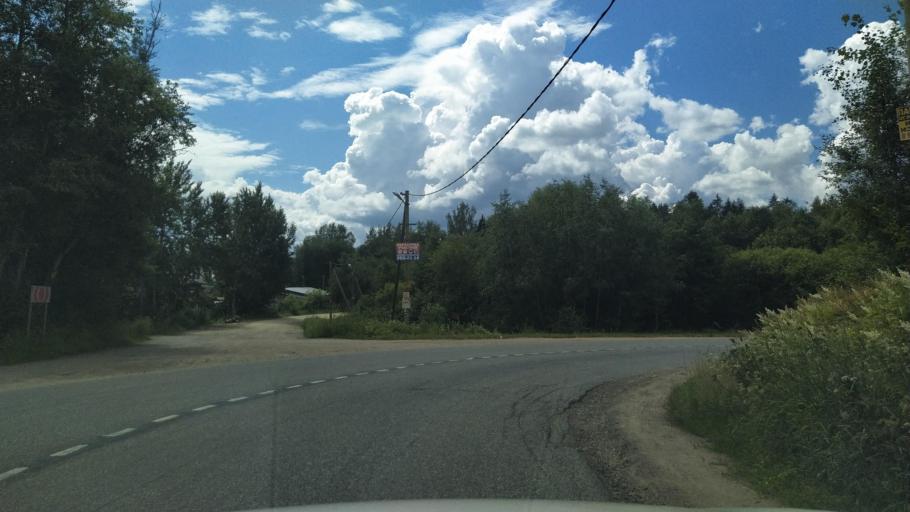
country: RU
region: Leningrad
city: Rozhdestveno
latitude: 59.3443
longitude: 29.9496
